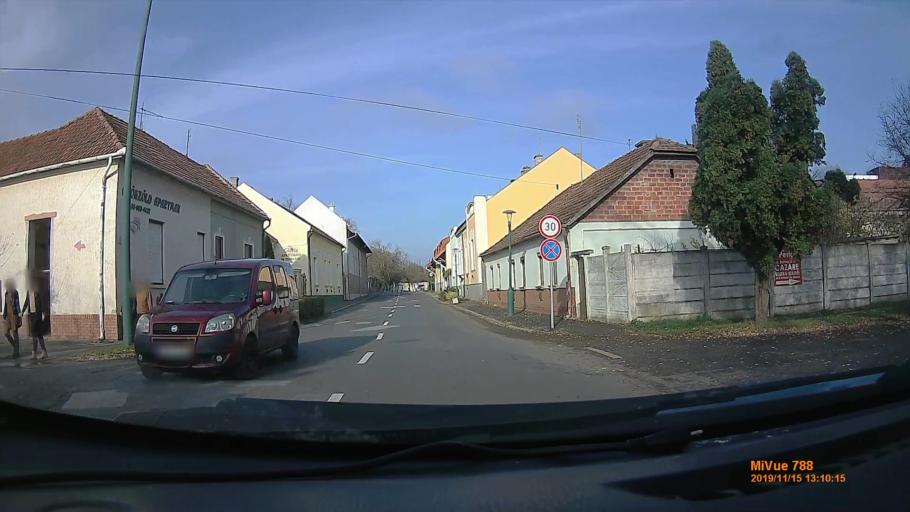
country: HU
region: Bekes
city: Gyula
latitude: 46.6430
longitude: 21.2801
